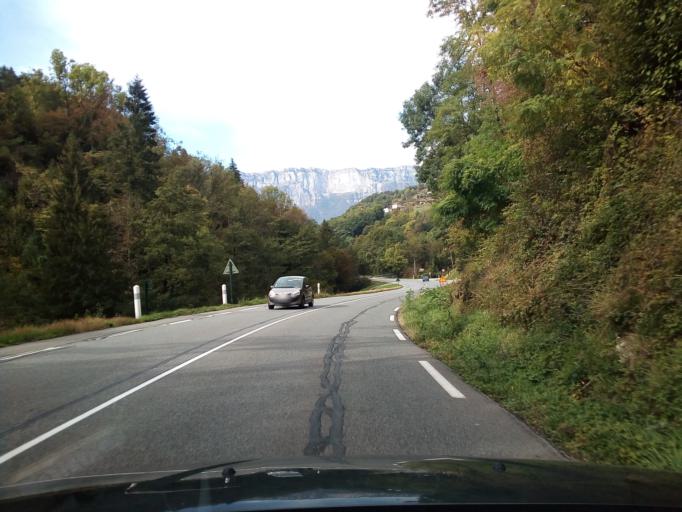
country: FR
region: Rhone-Alpes
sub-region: Departement de l'Isere
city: Le Cheylas
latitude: 45.3670
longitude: 6.0209
